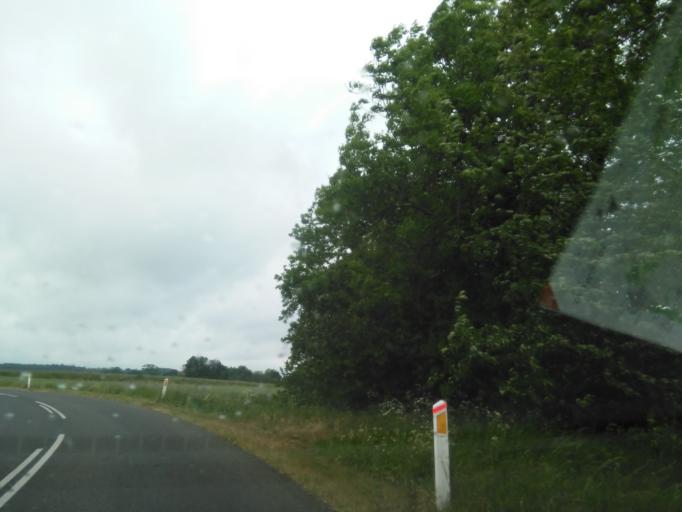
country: DK
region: Capital Region
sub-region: Bornholm Kommune
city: Ronne
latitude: 55.2400
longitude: 14.7456
